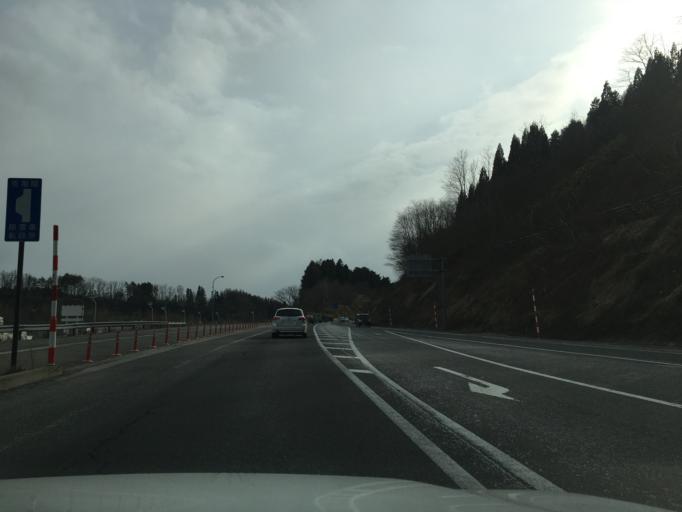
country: JP
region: Aomori
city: Namioka
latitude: 40.7734
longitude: 140.5991
